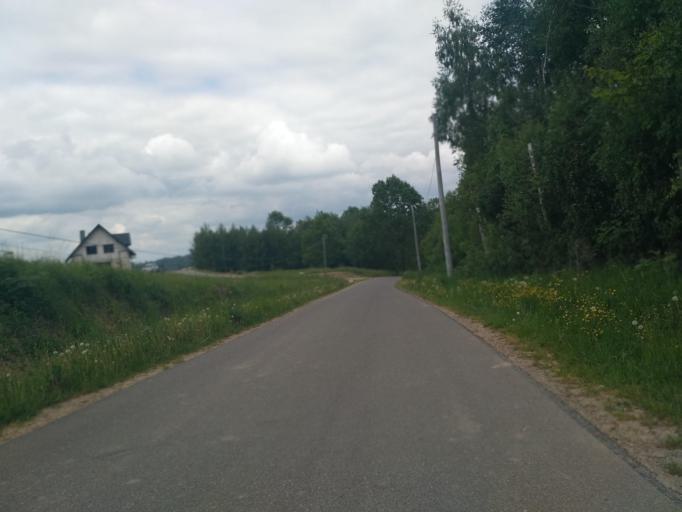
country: PL
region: Subcarpathian Voivodeship
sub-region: Powiat jasielski
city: Tarnowiec
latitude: 49.7018
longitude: 21.5805
